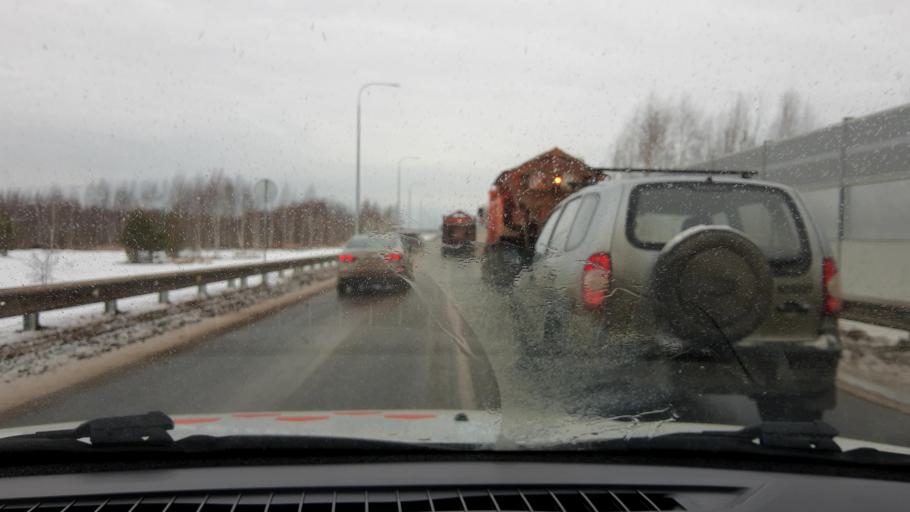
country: RU
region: Nizjnij Novgorod
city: Neklyudovo
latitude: 56.4243
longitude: 43.9778
